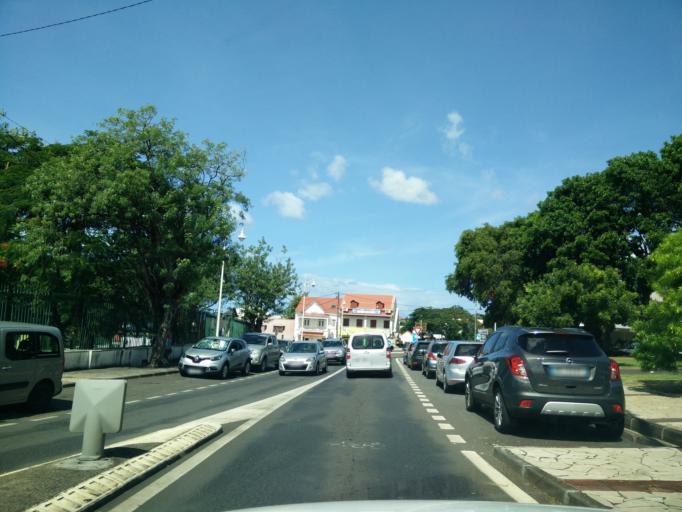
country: GP
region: Guadeloupe
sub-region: Guadeloupe
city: Basse-Terre
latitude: 15.9941
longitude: -61.7267
